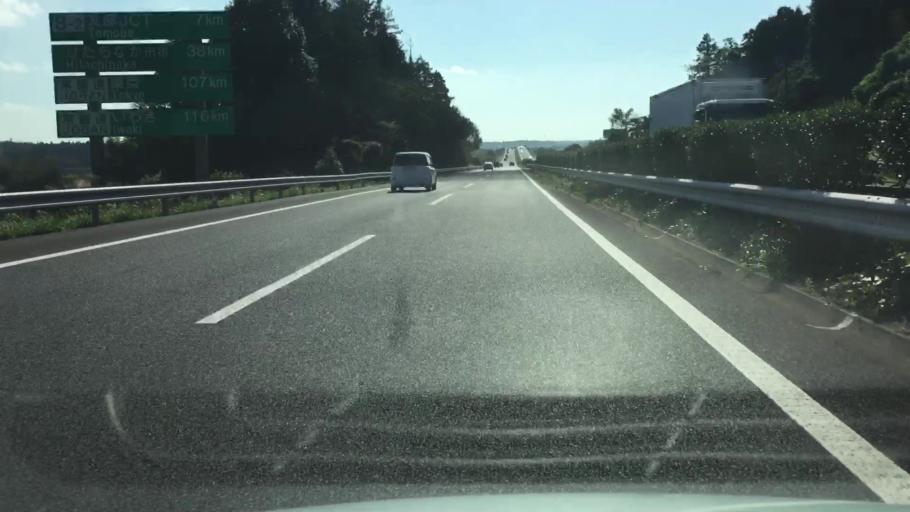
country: JP
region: Ibaraki
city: Tomobe
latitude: 36.3342
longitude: 140.2864
